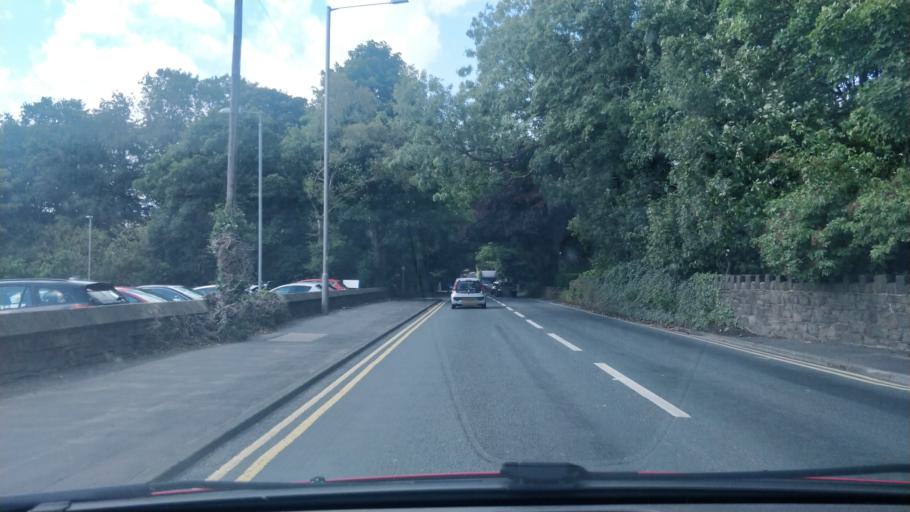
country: GB
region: England
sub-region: Lancashire
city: Appley Bridge
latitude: 53.5914
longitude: -2.7114
